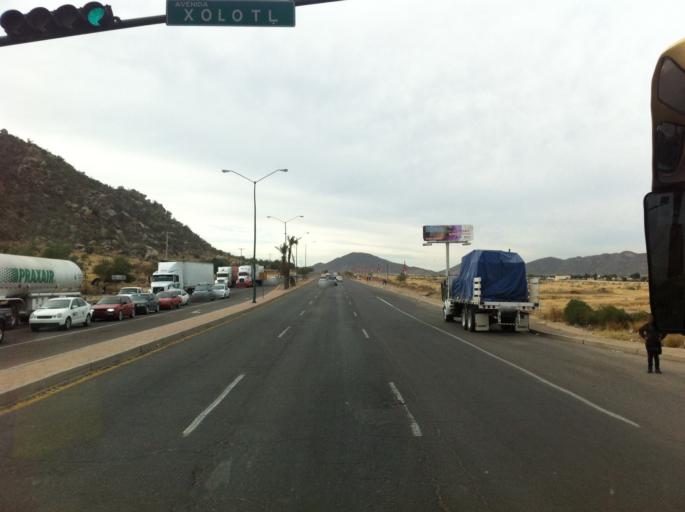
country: MX
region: Sonora
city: Hermosillo
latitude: 29.0256
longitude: -110.9606
